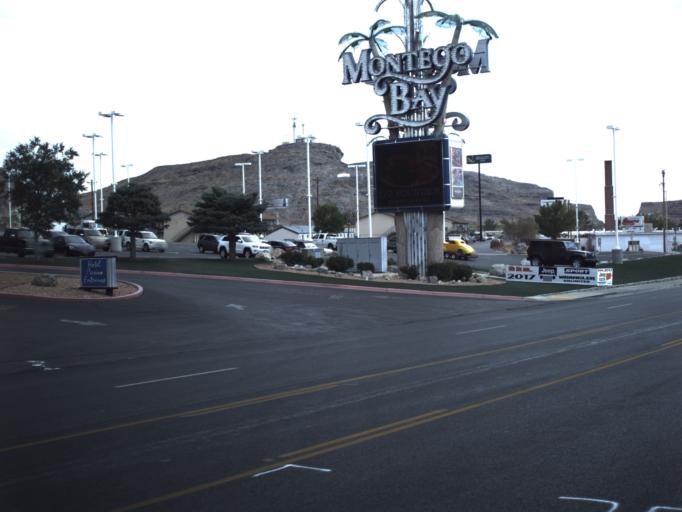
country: US
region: Utah
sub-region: Tooele County
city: Wendover
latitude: 40.7358
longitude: -114.0433
